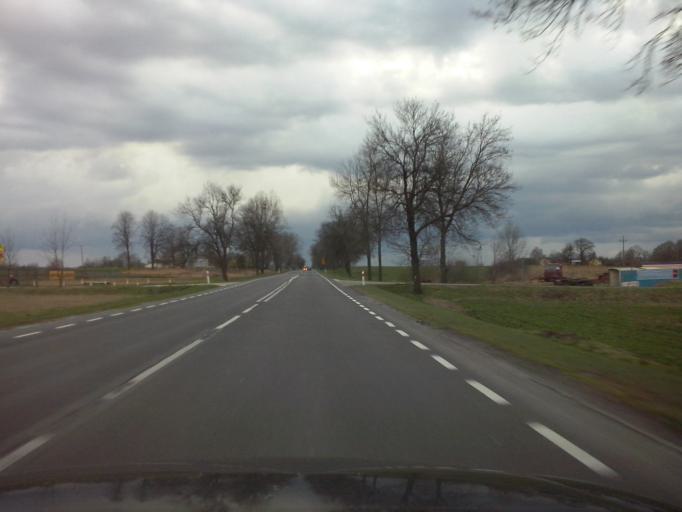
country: PL
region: Lublin Voivodeship
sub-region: Powiat chelmski
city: Rejowiec
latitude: 51.1693
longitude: 23.3312
